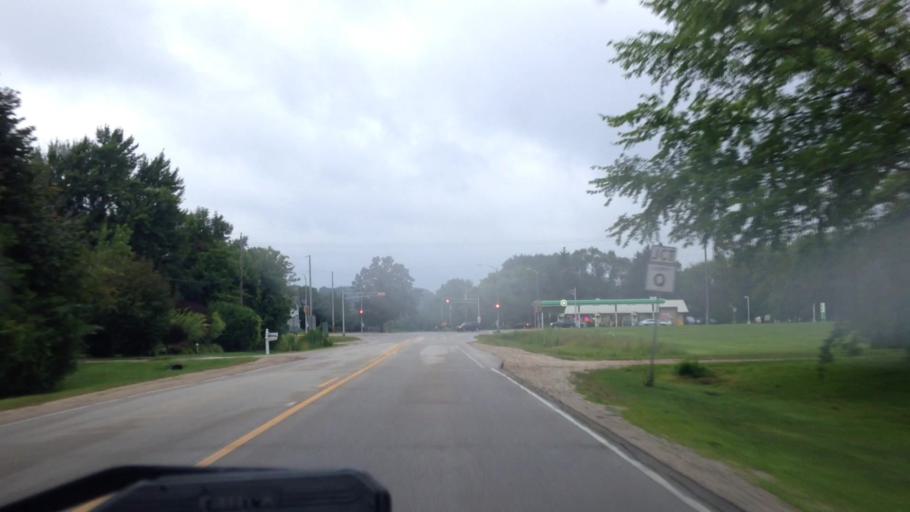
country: US
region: Wisconsin
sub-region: Waukesha County
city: Lannon
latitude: 43.1912
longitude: -88.1822
